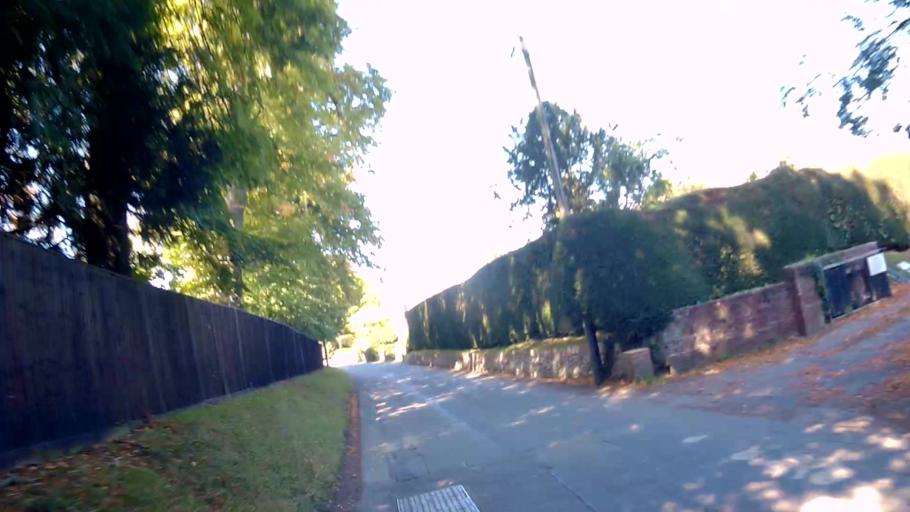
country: GB
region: England
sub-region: Hampshire
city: Overton
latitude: 51.2487
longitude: -1.1849
